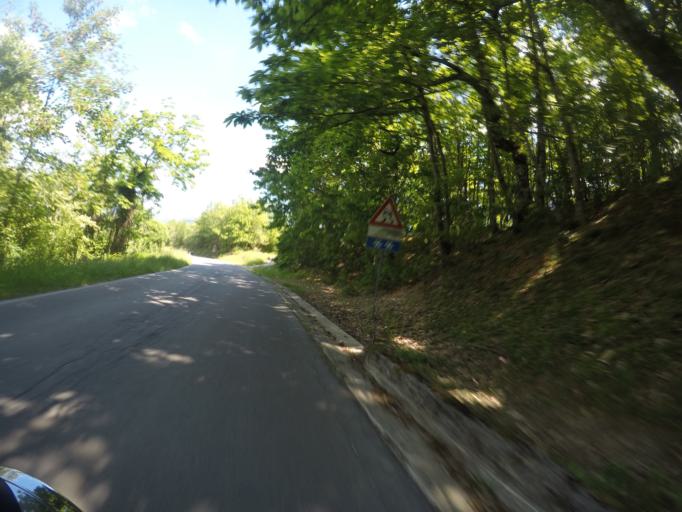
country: IT
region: Tuscany
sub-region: Provincia di Lucca
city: Careggine
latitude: 44.1226
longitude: 10.3302
